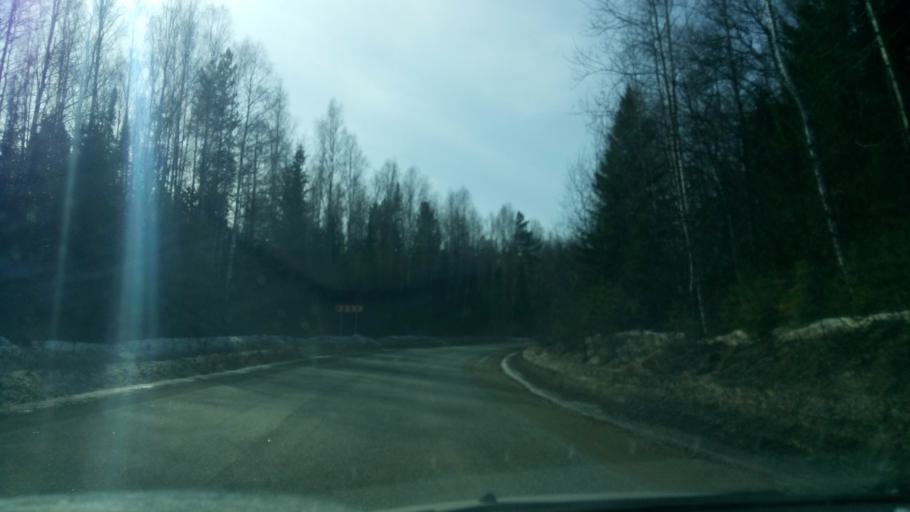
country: RU
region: Sverdlovsk
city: Chernoistochinsk
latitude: 57.6979
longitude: 59.7612
